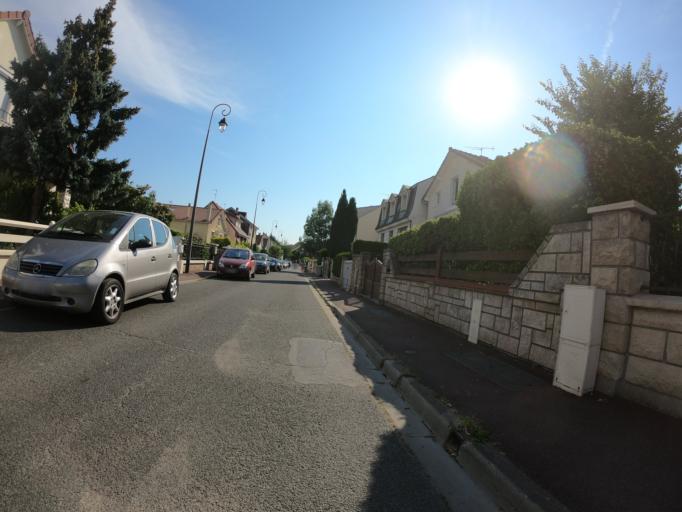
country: FR
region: Ile-de-France
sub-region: Departement des Hauts-de-Seine
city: Antony
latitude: 48.7422
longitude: 2.2930
